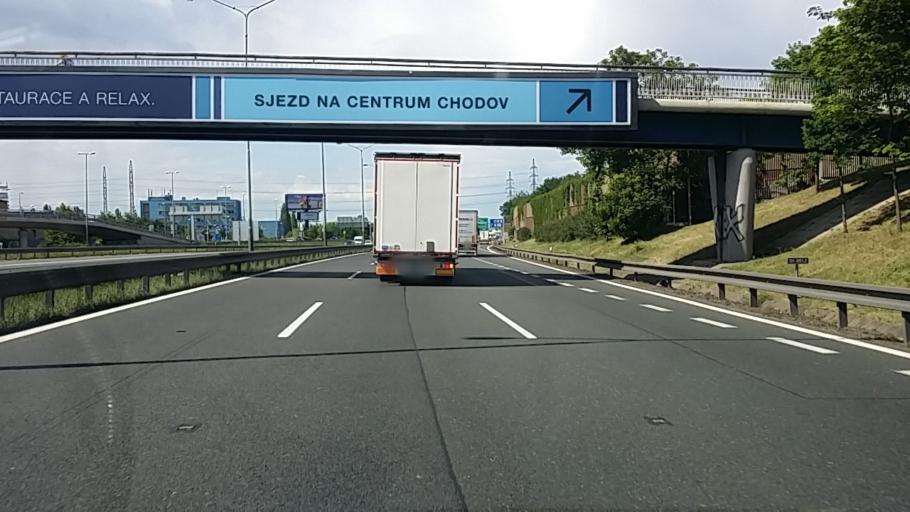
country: CZ
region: Central Bohemia
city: Vestec
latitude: 50.0311
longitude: 14.4936
